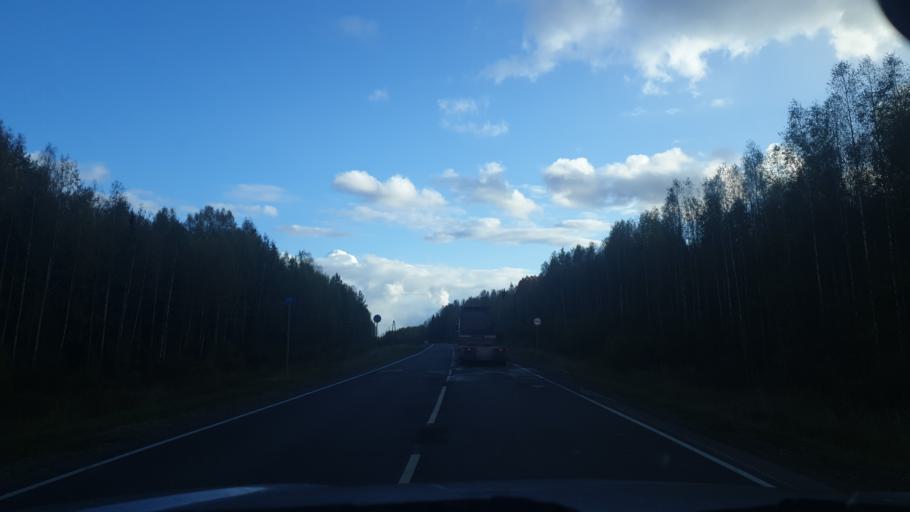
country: RU
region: Kirov
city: Murashi
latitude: 59.1637
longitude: 48.9890
